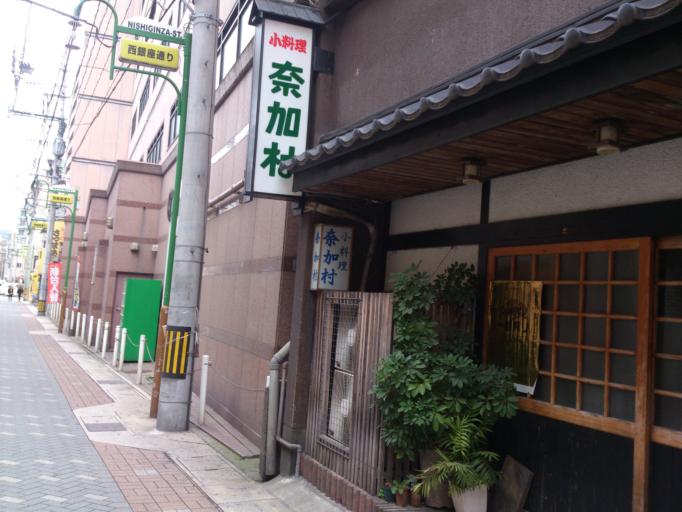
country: JP
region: Kagoshima
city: Kagoshima-shi
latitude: 31.5857
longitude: 130.5436
